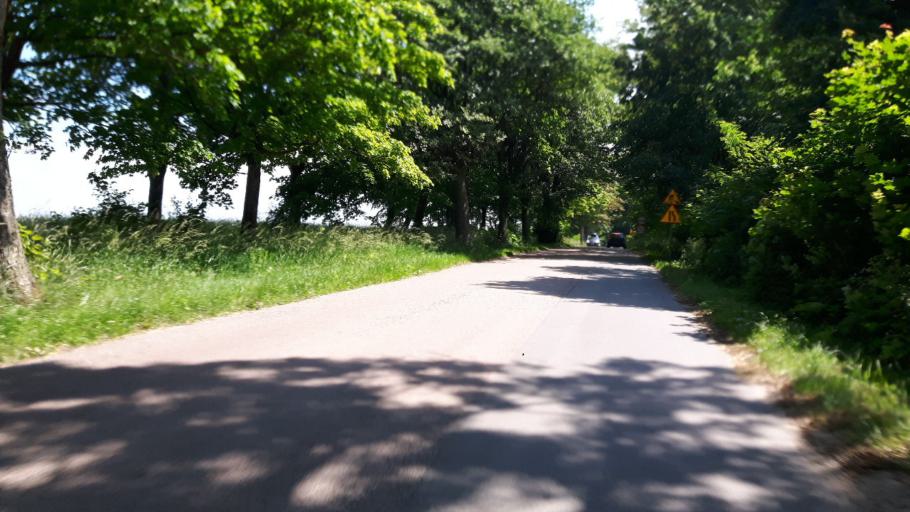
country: PL
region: Pomeranian Voivodeship
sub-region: Powiat wejherowski
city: Choczewo
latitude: 54.7459
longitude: 17.8031
